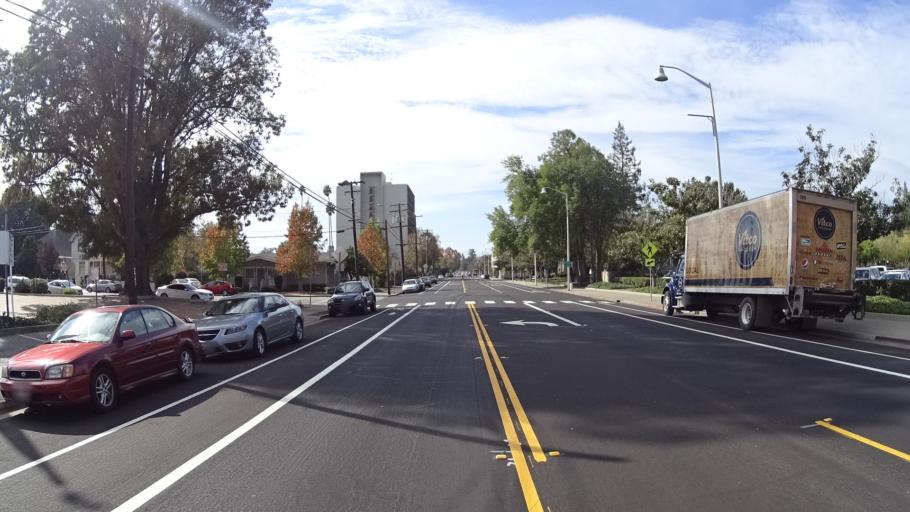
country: US
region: California
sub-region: Santa Clara County
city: Santa Clara
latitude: 37.3490
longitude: -121.9436
